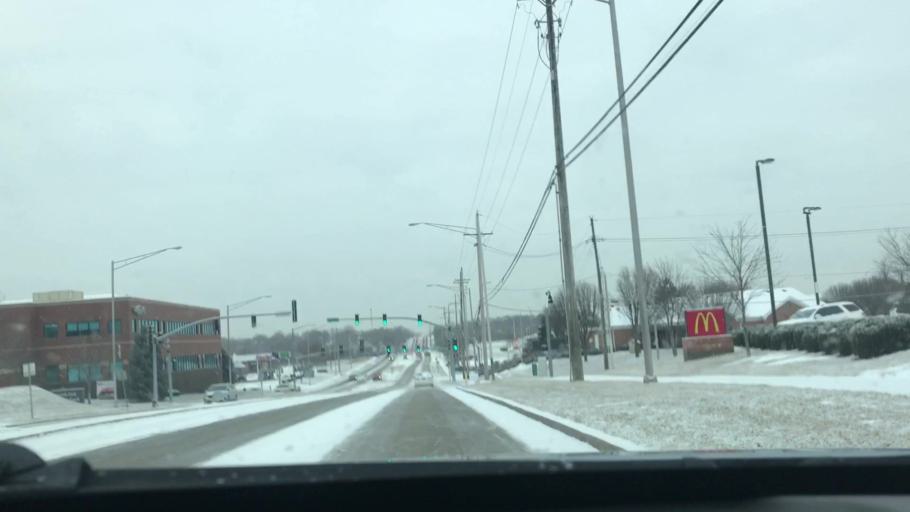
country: US
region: Missouri
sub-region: Clay County
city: Gladstone
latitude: 39.2657
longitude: -94.5758
